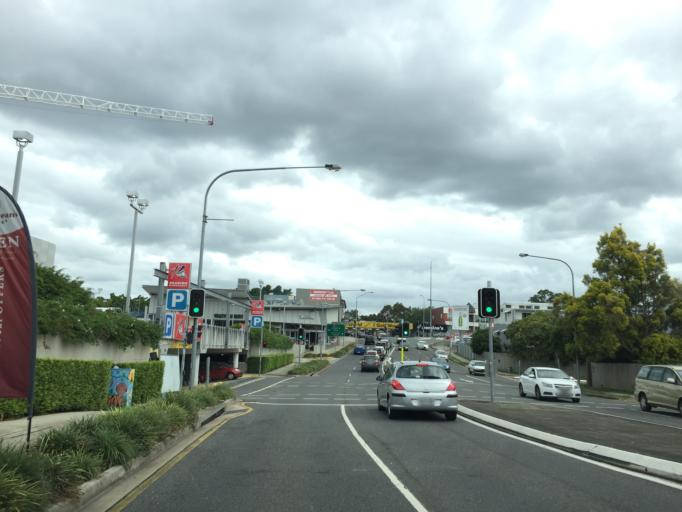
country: AU
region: Queensland
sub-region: Brisbane
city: Wilston
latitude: -27.4365
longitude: 153.0084
